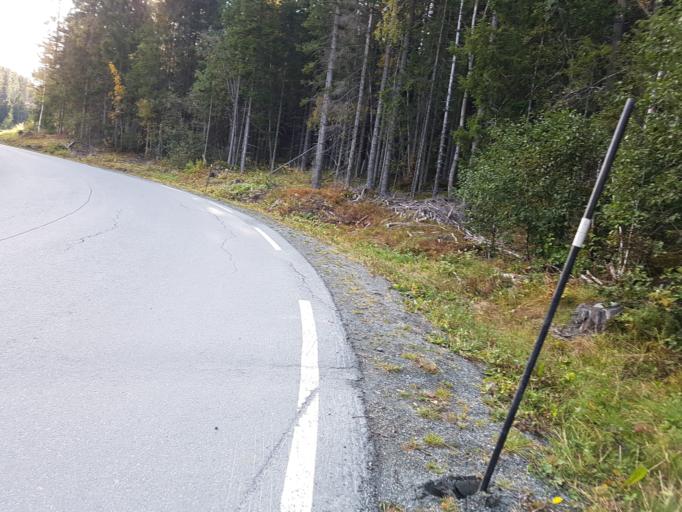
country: NO
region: Sor-Trondelag
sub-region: Klaebu
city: Klaebu
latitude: 63.3477
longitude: 10.5371
